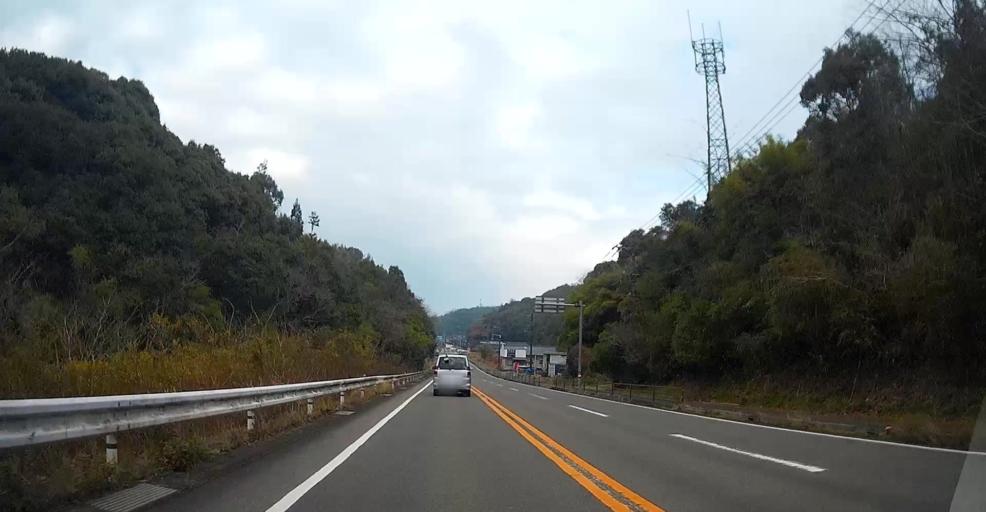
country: JP
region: Kumamoto
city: Yatsushiro
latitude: 32.5603
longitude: 130.4143
